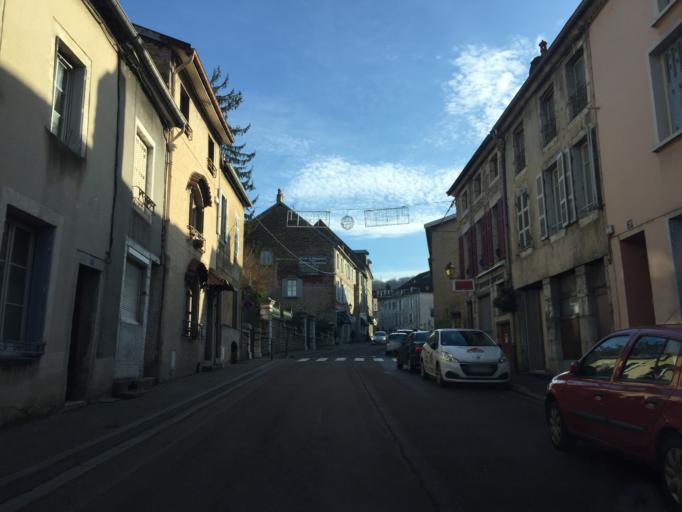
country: FR
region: Franche-Comte
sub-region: Departement du Jura
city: Arbois
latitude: 46.9053
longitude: 5.7706
